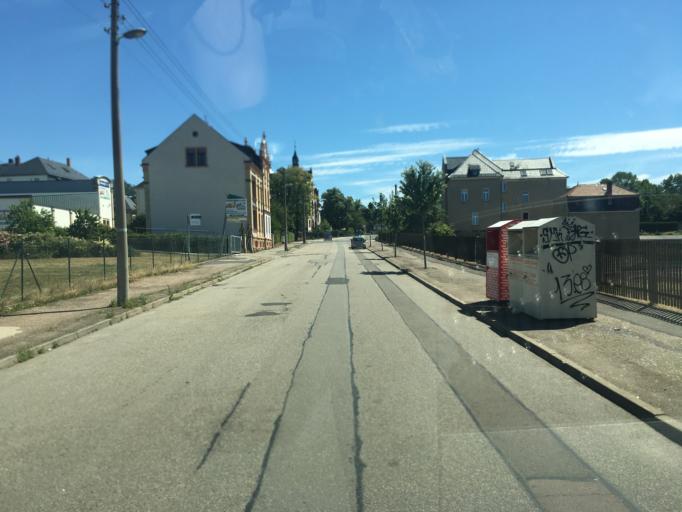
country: DE
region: Saxony
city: Frankenberg
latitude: 50.9147
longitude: 13.0424
